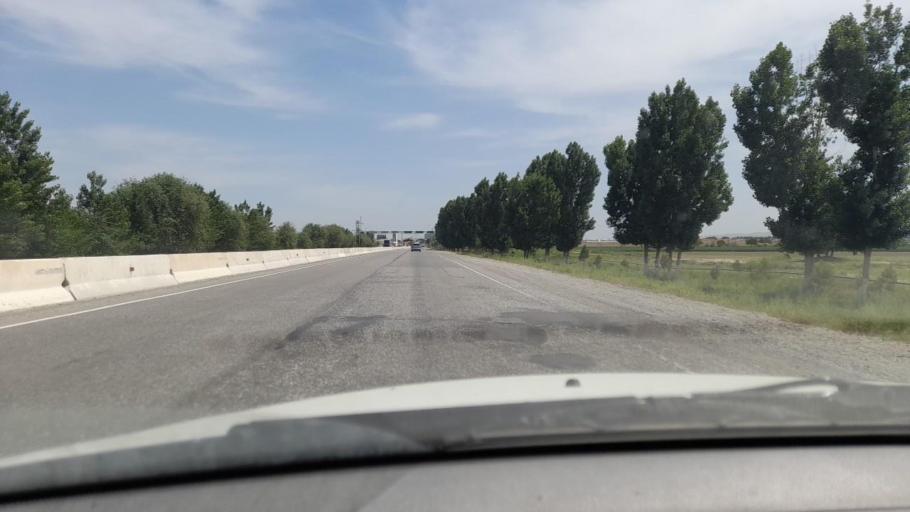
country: UZ
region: Navoiy
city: Karmana Shahri
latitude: 40.1209
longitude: 65.4826
